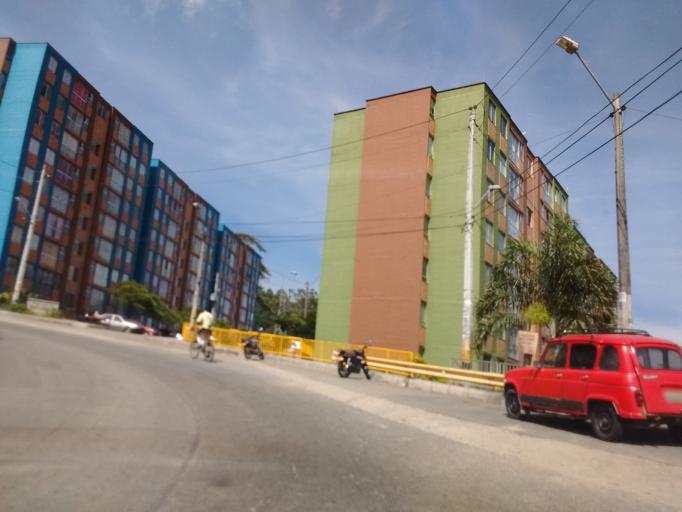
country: CO
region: Antioquia
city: Medellin
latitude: 6.2305
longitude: -75.5368
